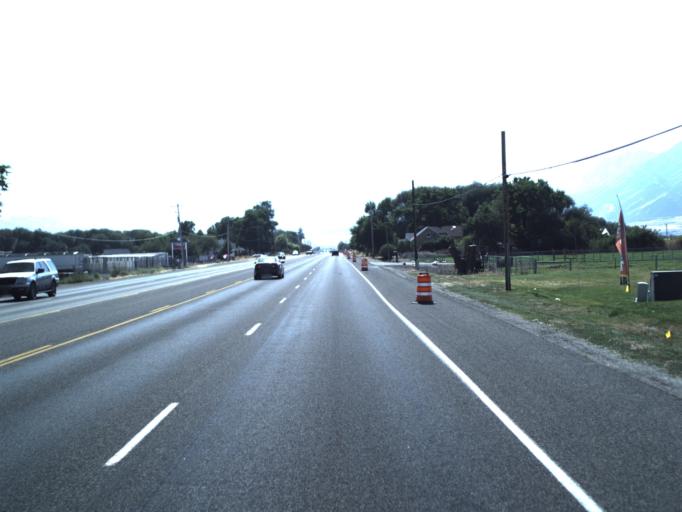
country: US
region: Utah
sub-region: Cache County
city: Nibley
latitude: 41.6827
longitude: -111.8760
